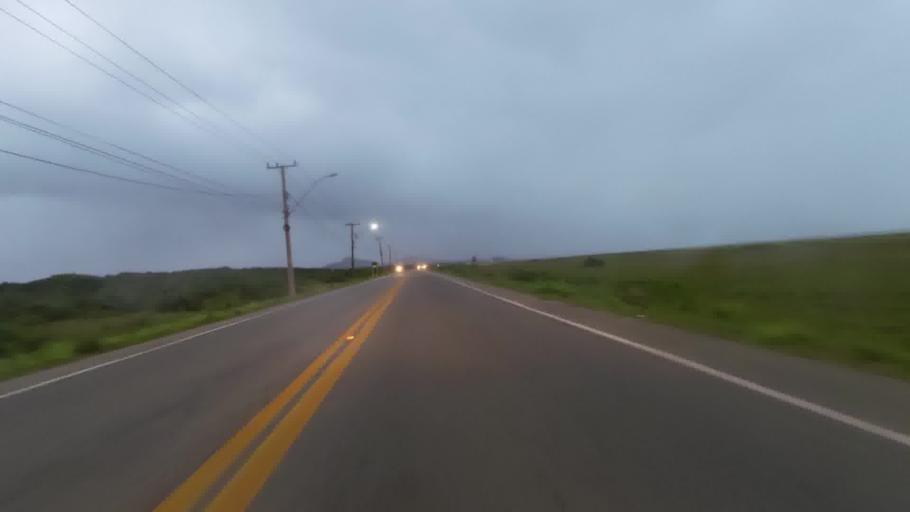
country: BR
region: Espirito Santo
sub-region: Itapemirim
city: Itapemirim
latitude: -20.9656
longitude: -40.8105
